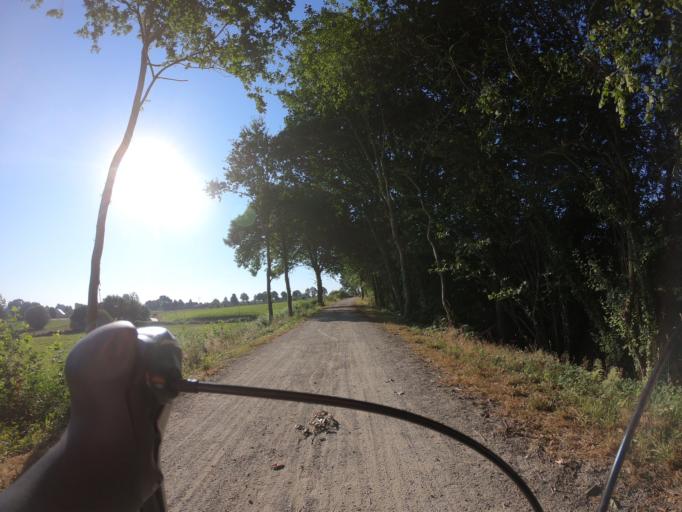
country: FR
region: Lower Normandy
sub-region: Departement de la Manche
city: Isigny-le-Buat
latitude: 48.6053
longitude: -1.1299
